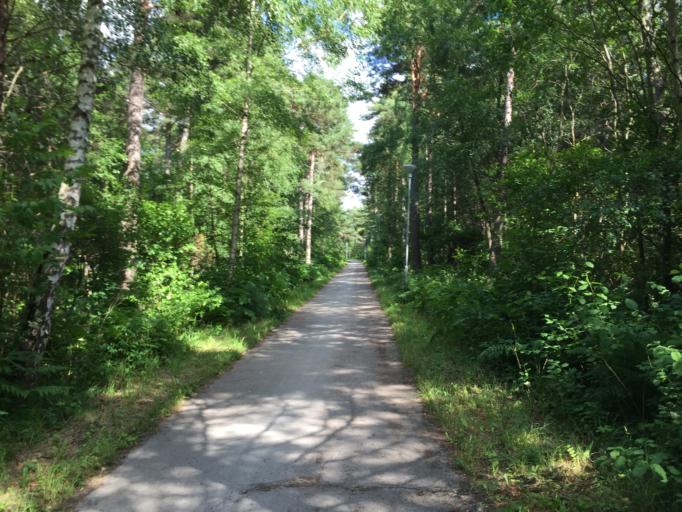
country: SE
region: Gotland
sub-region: Gotland
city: Visby
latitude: 57.6106
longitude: 18.2892
